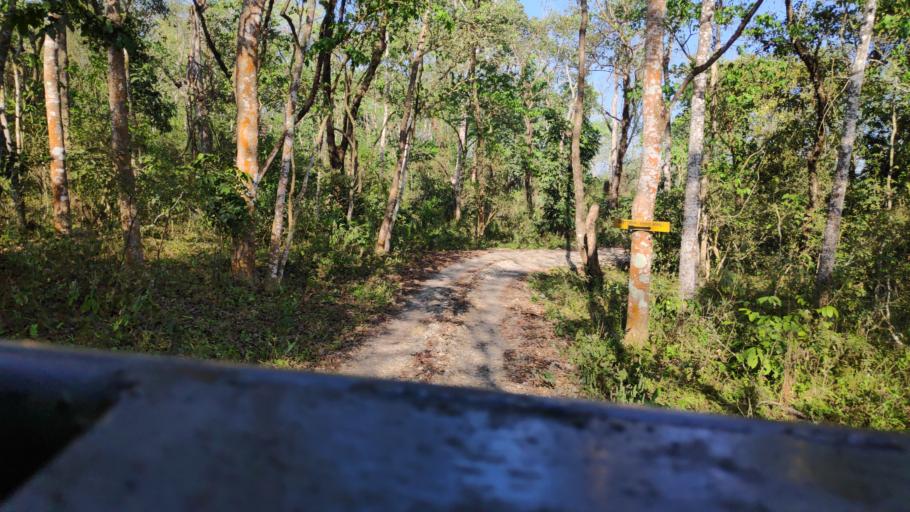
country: NP
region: Central Region
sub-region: Narayani Zone
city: Bharatpur
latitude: 27.5612
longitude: 84.5332
